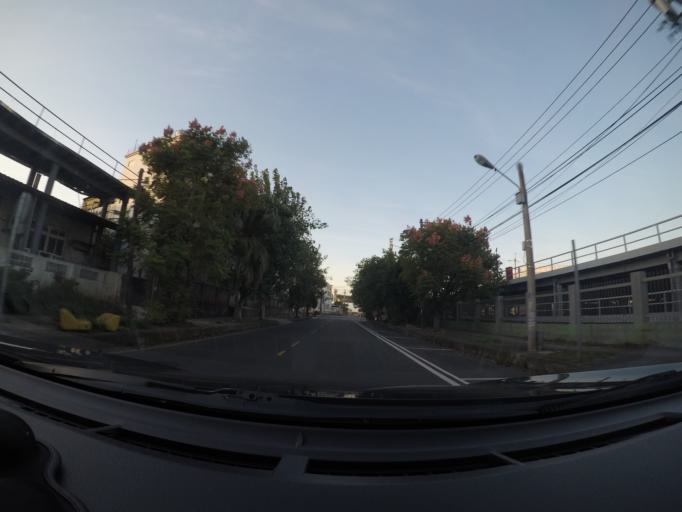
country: TW
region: Taiwan
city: Taoyuan City
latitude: 24.9925
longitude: 121.2458
